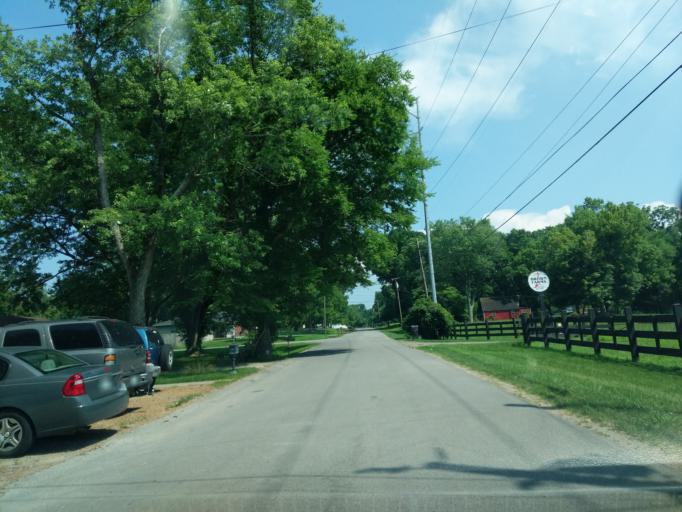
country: US
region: Tennessee
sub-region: Davidson County
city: Lakewood
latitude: 36.2793
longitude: -86.6761
